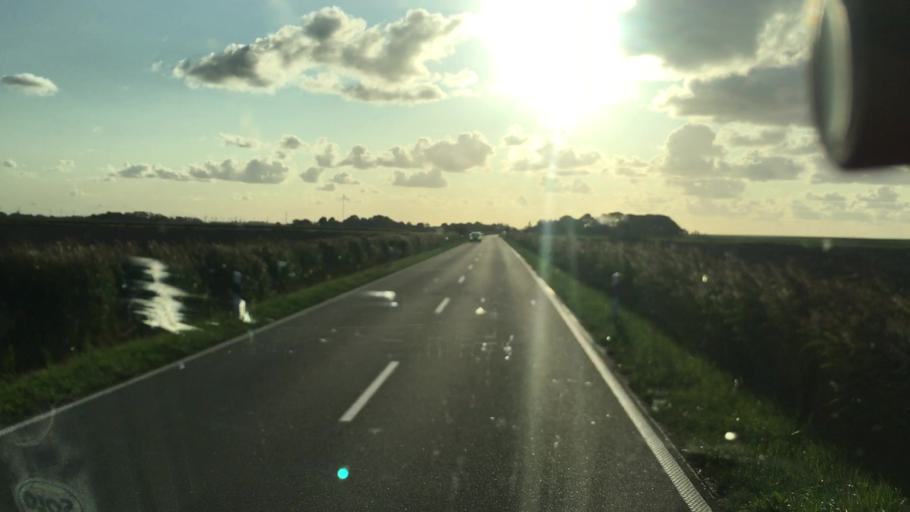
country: DE
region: Lower Saxony
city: Neuharlingersiel
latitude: 53.6897
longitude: 7.6795
